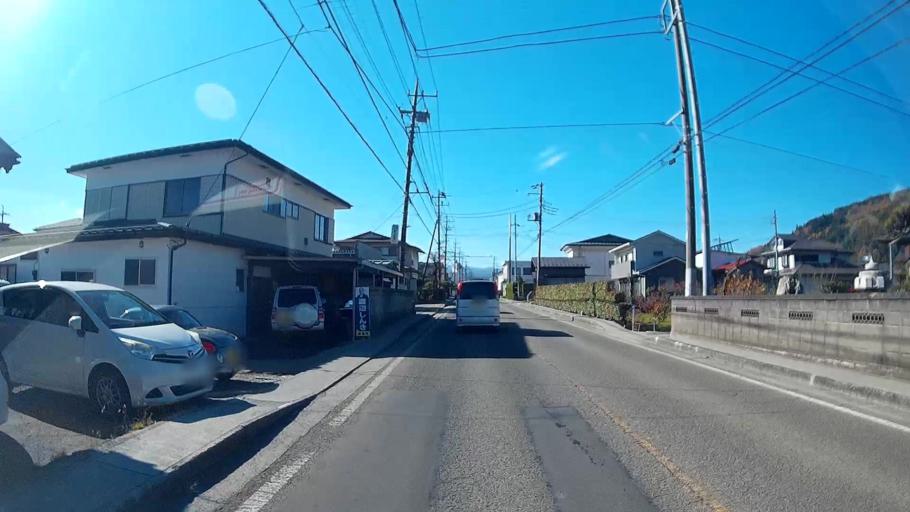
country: JP
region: Yamanashi
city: Fujikawaguchiko
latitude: 35.5013
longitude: 138.8146
